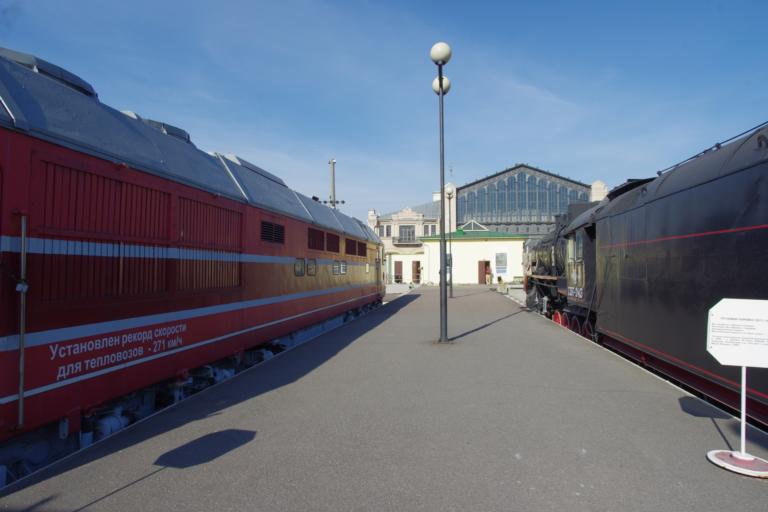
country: RU
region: St.-Petersburg
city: Admiralteisky
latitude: 59.9046
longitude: 30.3071
